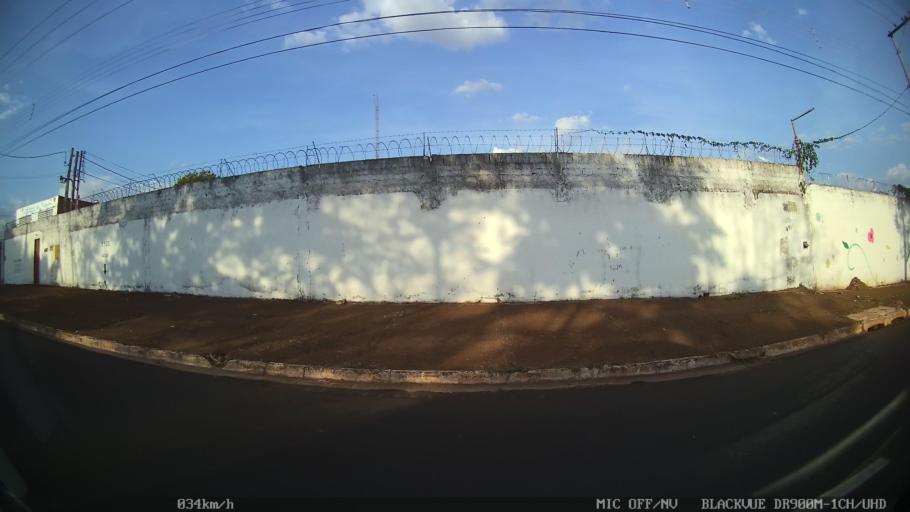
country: BR
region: Sao Paulo
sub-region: Ribeirao Preto
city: Ribeirao Preto
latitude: -21.1285
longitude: -47.8029
